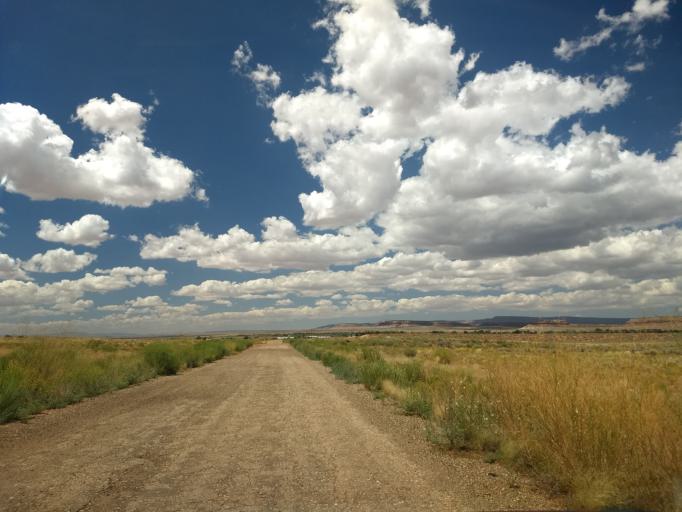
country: US
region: Arizona
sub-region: Coconino County
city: Fredonia
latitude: 36.9440
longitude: -112.5062
